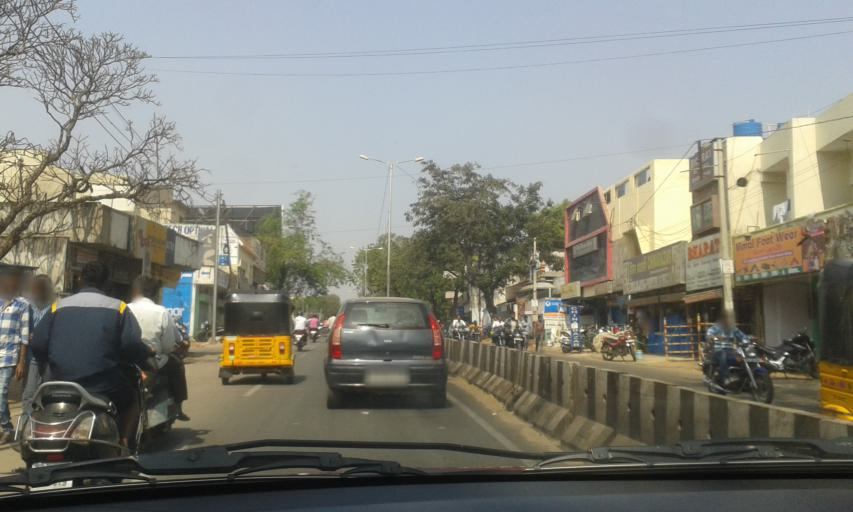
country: IN
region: Telangana
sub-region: Rangareddi
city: Secunderabad
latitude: 17.4943
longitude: 78.5127
